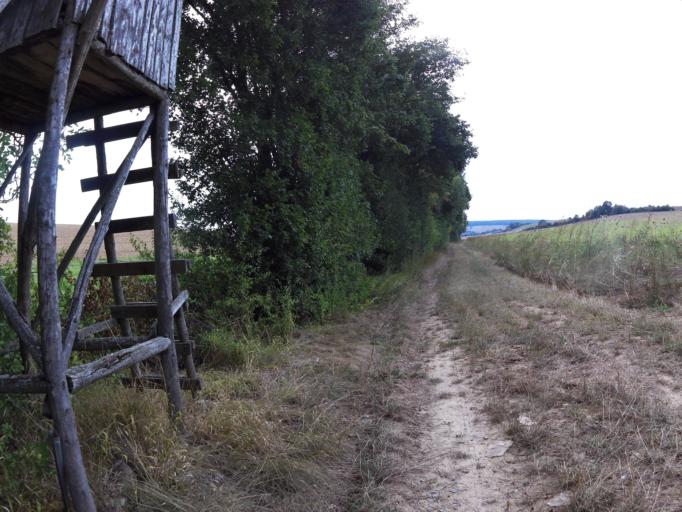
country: DE
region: Bavaria
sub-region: Regierungsbezirk Unterfranken
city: Kleinrinderfeld
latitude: 49.7118
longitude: 9.8316
